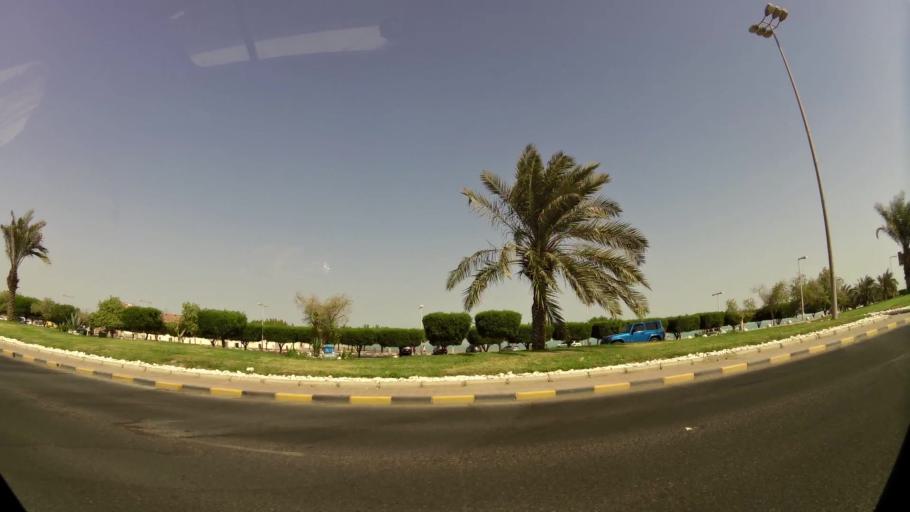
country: KW
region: Muhafazat Hawalli
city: Hawalli
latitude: 29.3460
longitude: 48.0408
